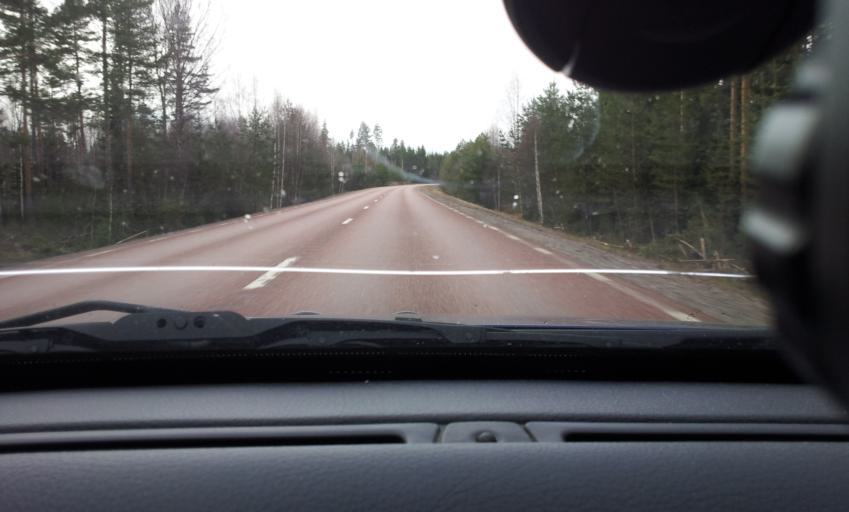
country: SE
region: Gaevleborg
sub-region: Ljusdals Kommun
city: Farila
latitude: 61.8145
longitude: 15.7646
